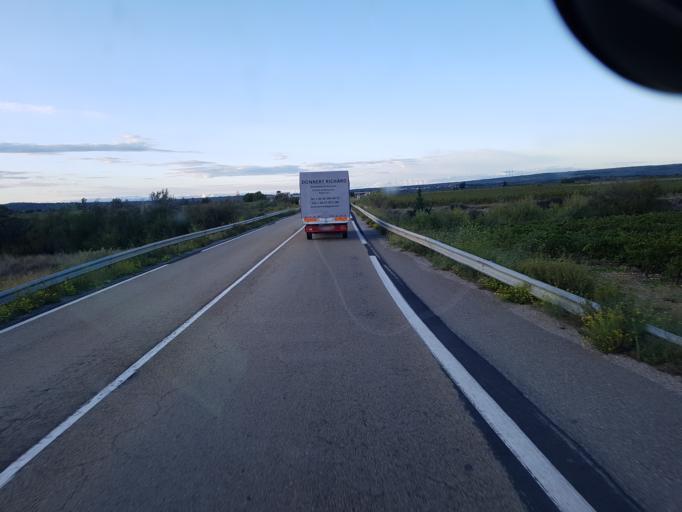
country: FR
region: Languedoc-Roussillon
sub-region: Departement de l'Aude
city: Leucate
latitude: 42.9392
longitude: 2.9905
